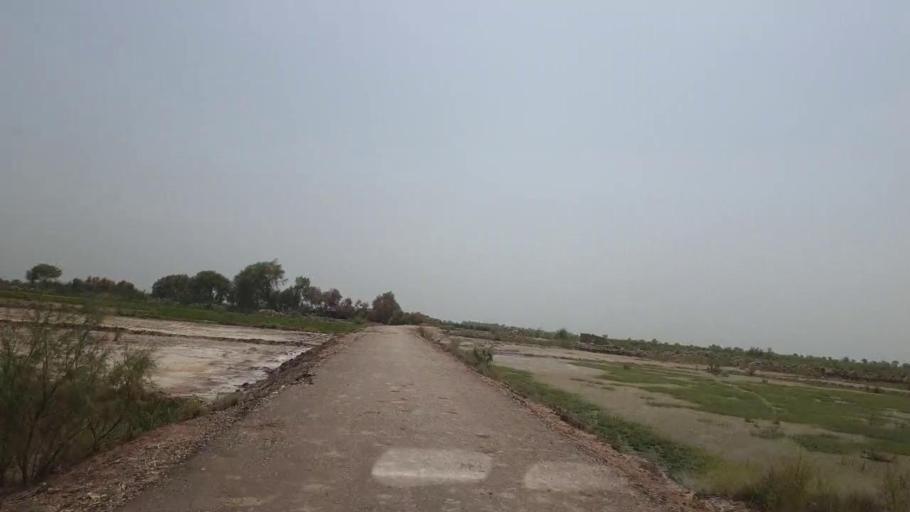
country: PK
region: Sindh
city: Garhi Yasin
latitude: 28.0572
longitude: 68.3164
